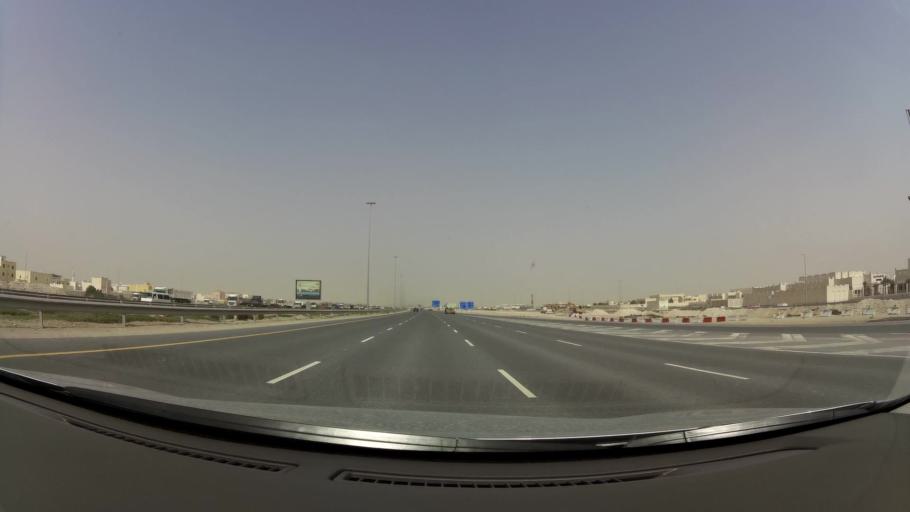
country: QA
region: Baladiyat ar Rayyan
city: Ar Rayyan
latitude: 25.1872
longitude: 51.3658
